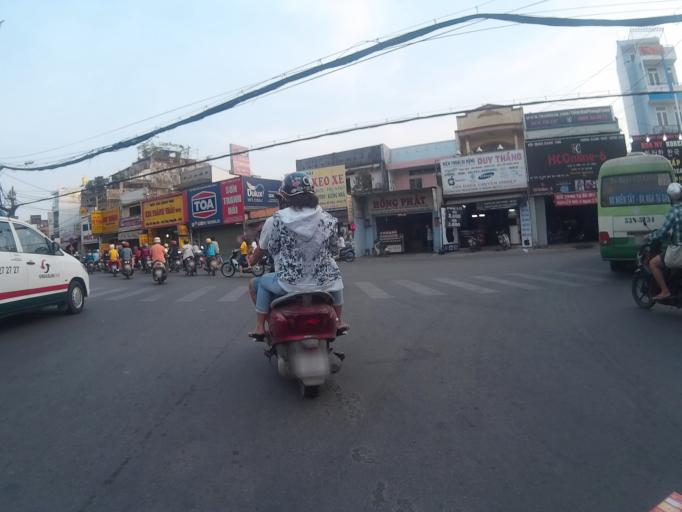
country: VN
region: Ho Chi Minh City
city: Ho Chi Minh City
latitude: 10.8038
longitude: 106.6326
